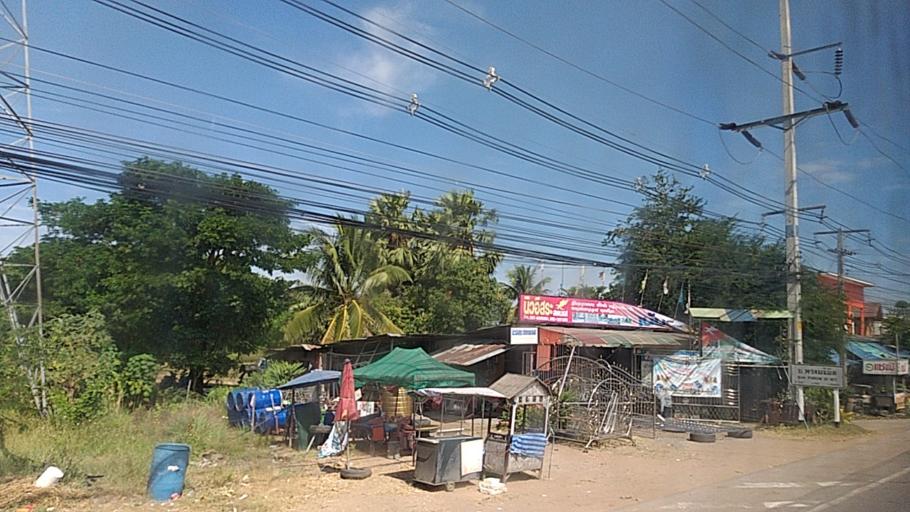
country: TH
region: Khon Kaen
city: Khon Kaen
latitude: 16.4429
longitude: 102.9462
